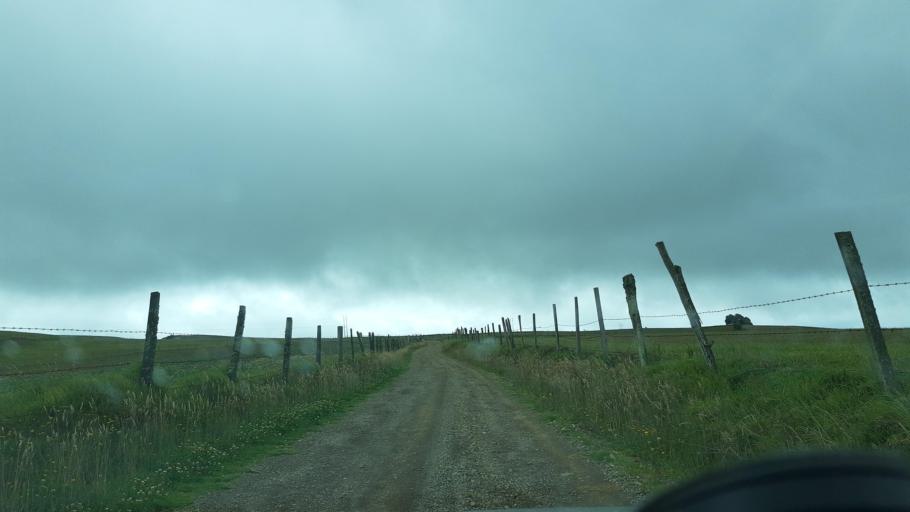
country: CO
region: Boyaca
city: Cucaita
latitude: 5.5114
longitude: -73.4417
